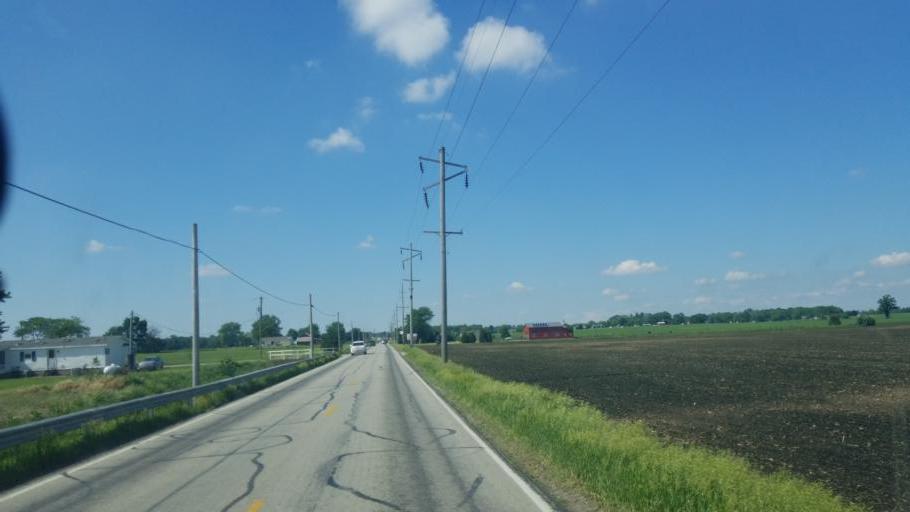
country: US
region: Indiana
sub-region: Elkhart County
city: Nappanee
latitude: 41.4160
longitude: -86.0011
